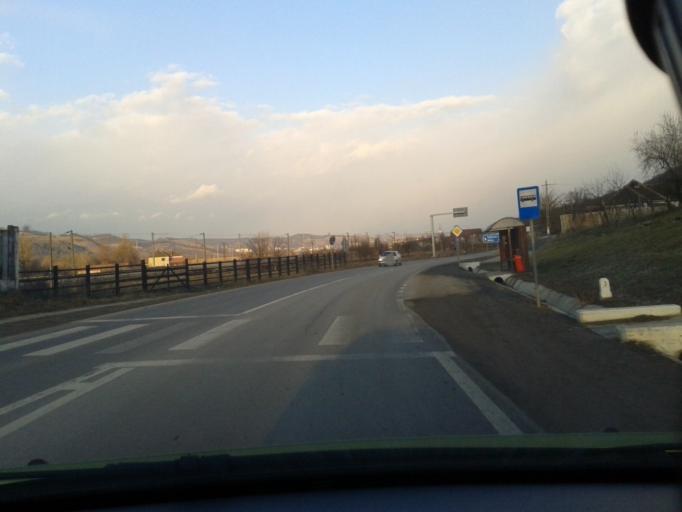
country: RO
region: Sibiu
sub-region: Comuna Tarnava
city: Tarnava
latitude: 46.1336
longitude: 24.2991
